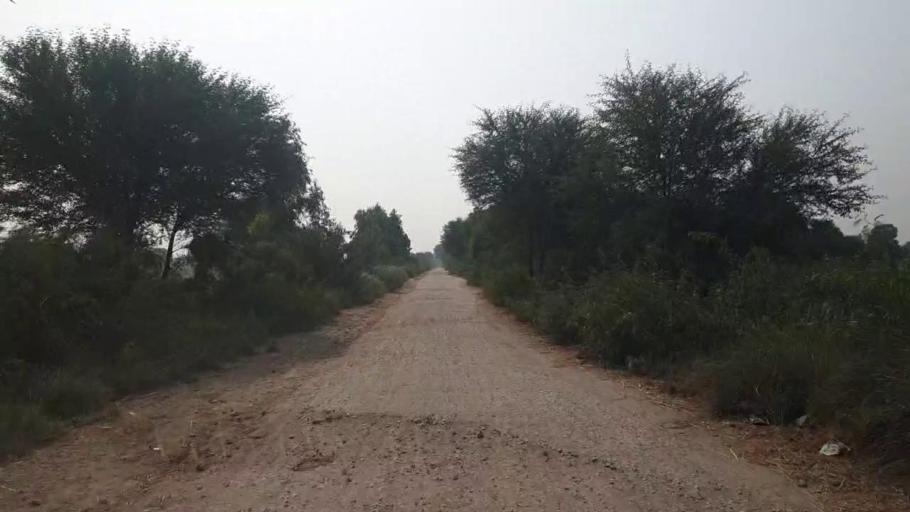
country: PK
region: Sindh
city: Tando Muhammad Khan
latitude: 25.2407
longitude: 68.5710
